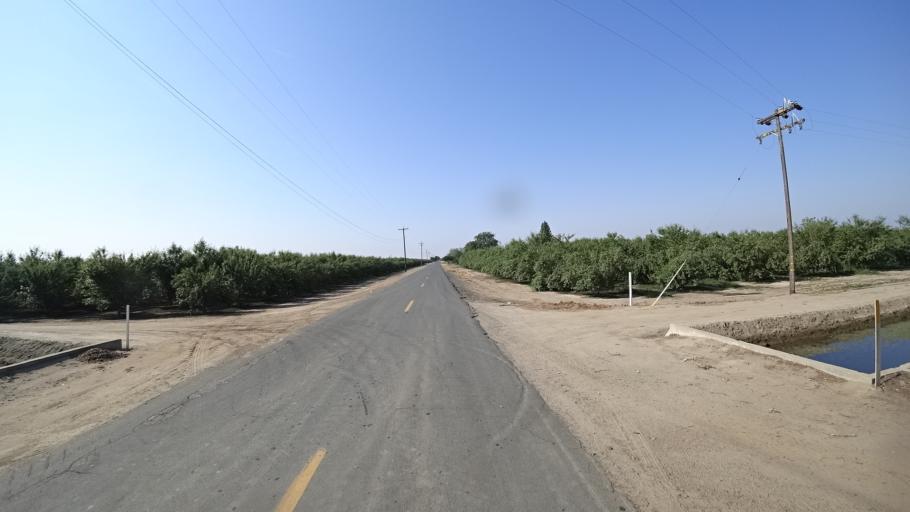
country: US
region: California
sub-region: Kings County
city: Lemoore
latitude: 36.3353
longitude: -119.8347
